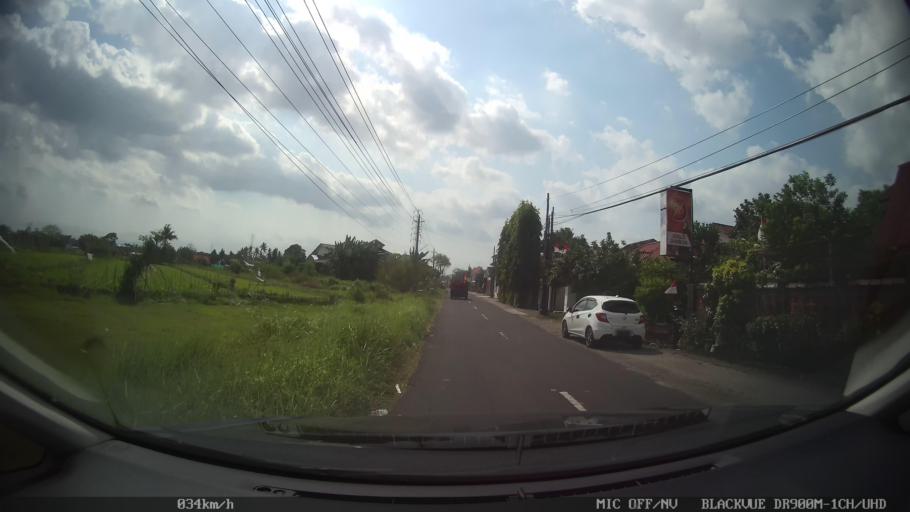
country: ID
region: Daerah Istimewa Yogyakarta
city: Yogyakarta
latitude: -7.7600
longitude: 110.3442
